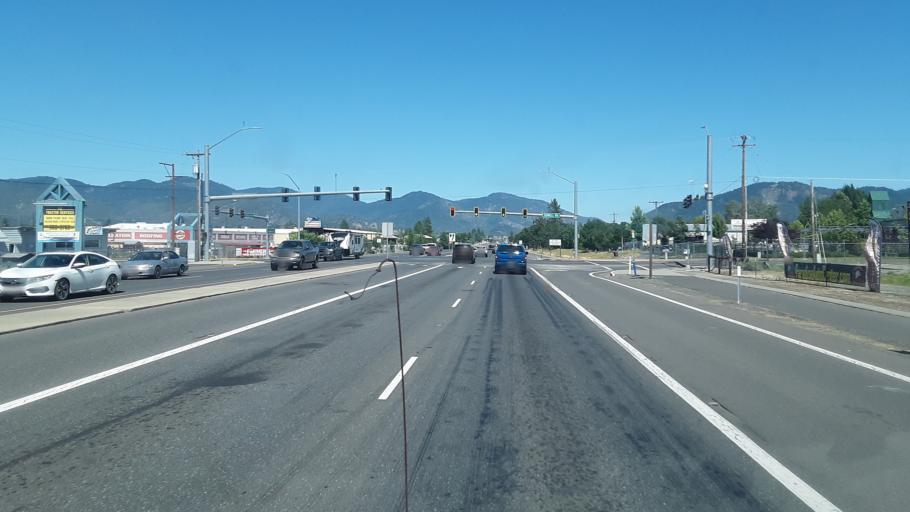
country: US
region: Oregon
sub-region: Josephine County
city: Redwood
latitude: 42.4183
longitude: -123.3680
